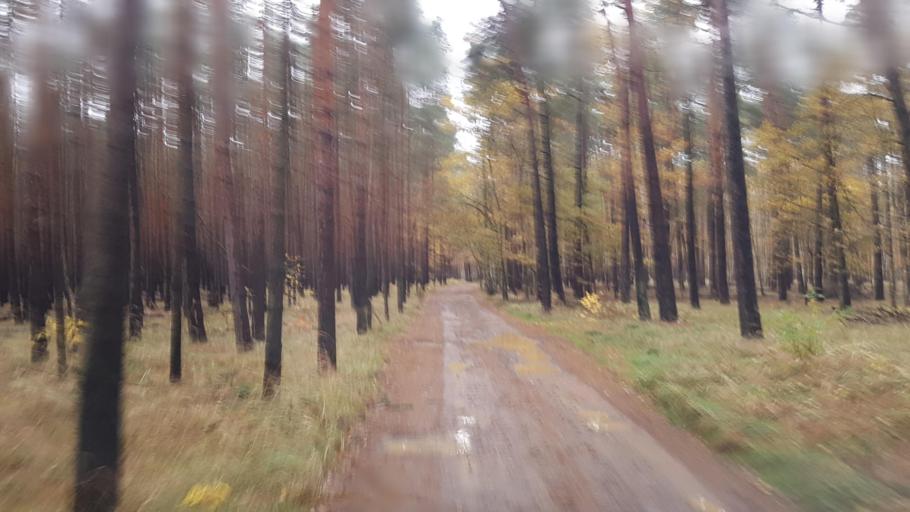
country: DE
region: Brandenburg
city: Drebkau
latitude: 51.6884
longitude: 14.2239
